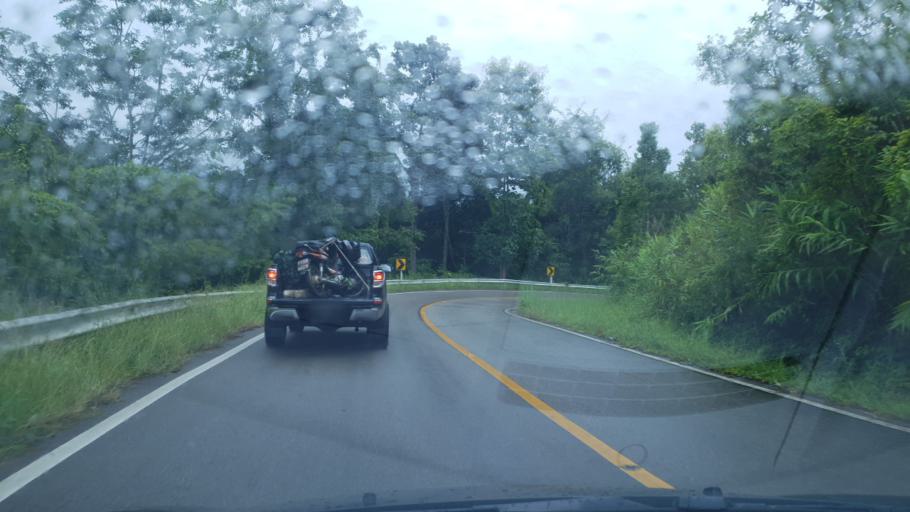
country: TH
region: Mae Hong Son
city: Mae La Noi
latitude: 18.5477
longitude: 97.9352
